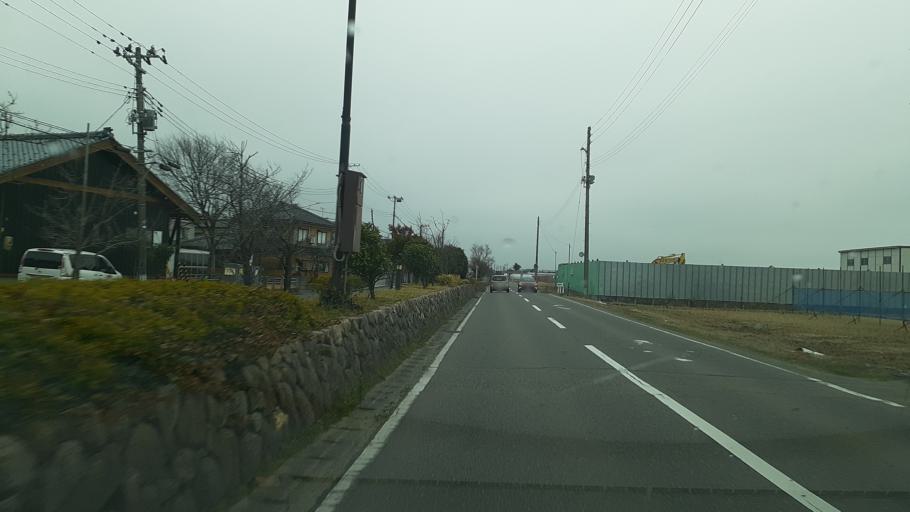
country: JP
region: Niigata
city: Niigata-shi
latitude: 37.8662
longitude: 139.0381
